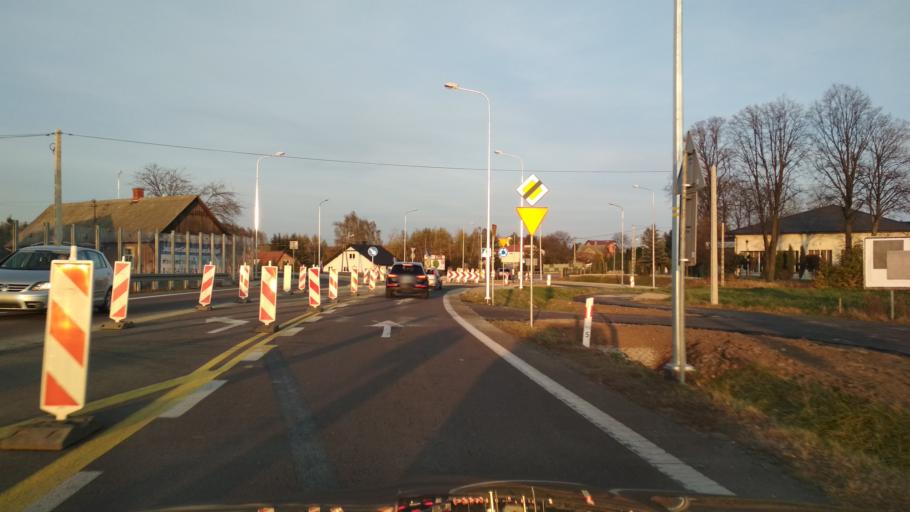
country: PL
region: Subcarpathian Voivodeship
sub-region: Powiat ropczycko-sedziszowski
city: Sedziszow Malopolski
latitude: 50.0692
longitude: 21.7404
